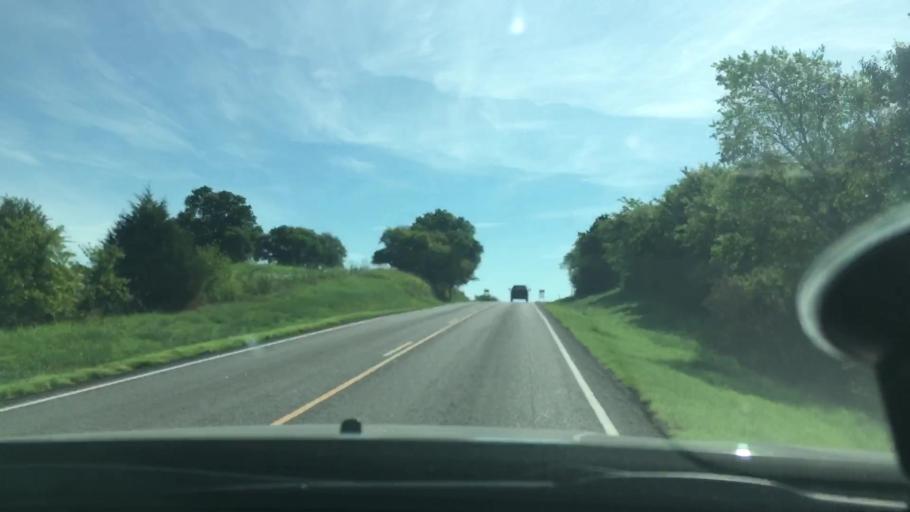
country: US
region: Oklahoma
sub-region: Carter County
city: Lone Grove
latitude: 34.3327
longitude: -97.2246
